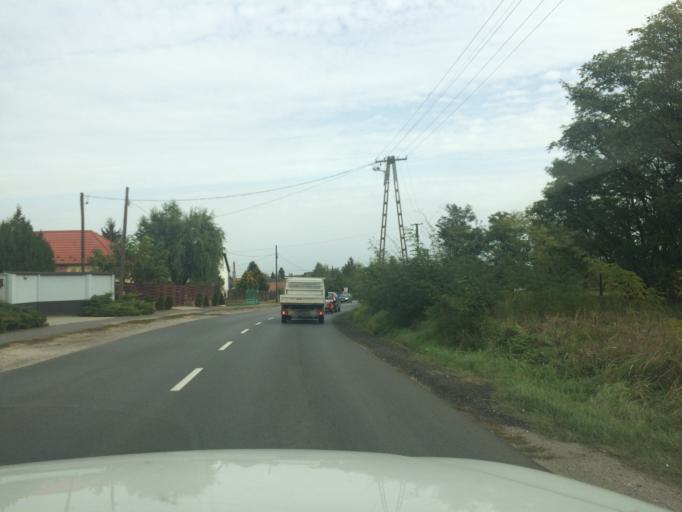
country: HU
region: Szabolcs-Szatmar-Bereg
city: Kotaj
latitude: 48.0181
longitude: 21.7394
